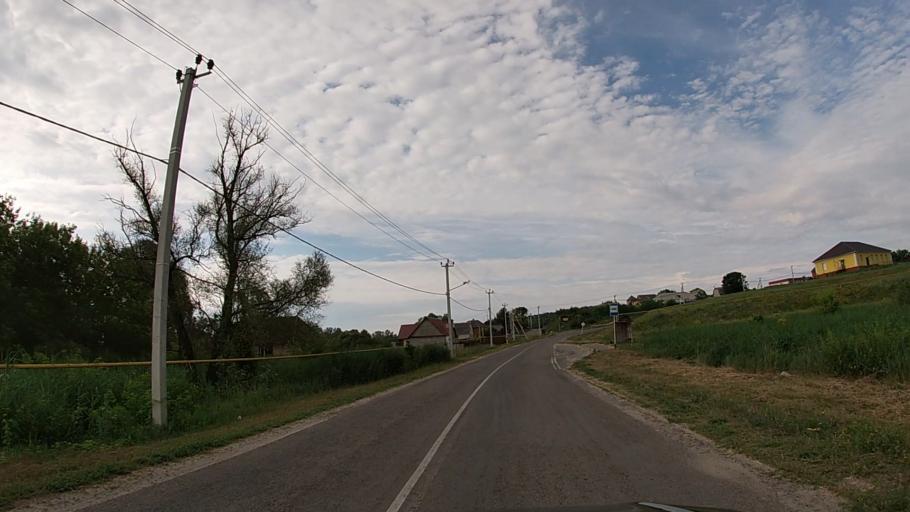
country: RU
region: Belgorod
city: Severnyy
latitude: 50.7077
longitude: 36.6006
